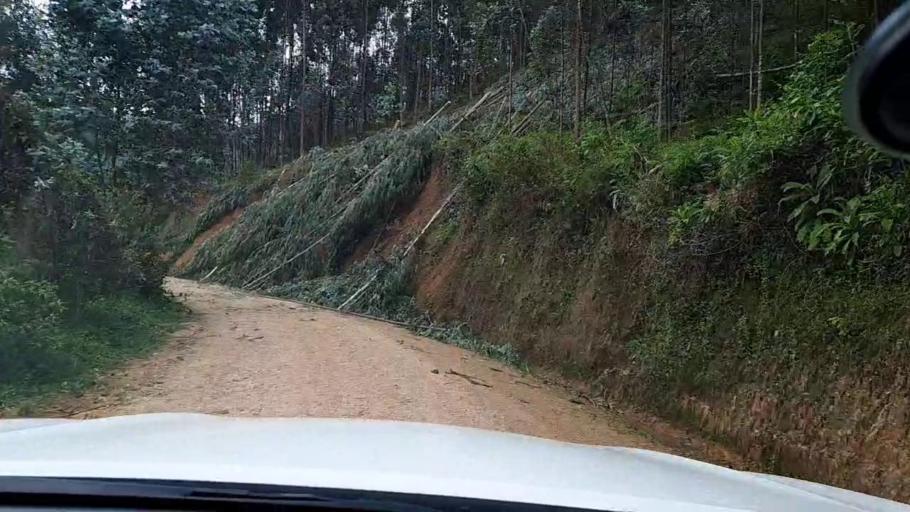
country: RW
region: Western Province
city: Kibuye
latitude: -2.2812
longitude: 29.3023
